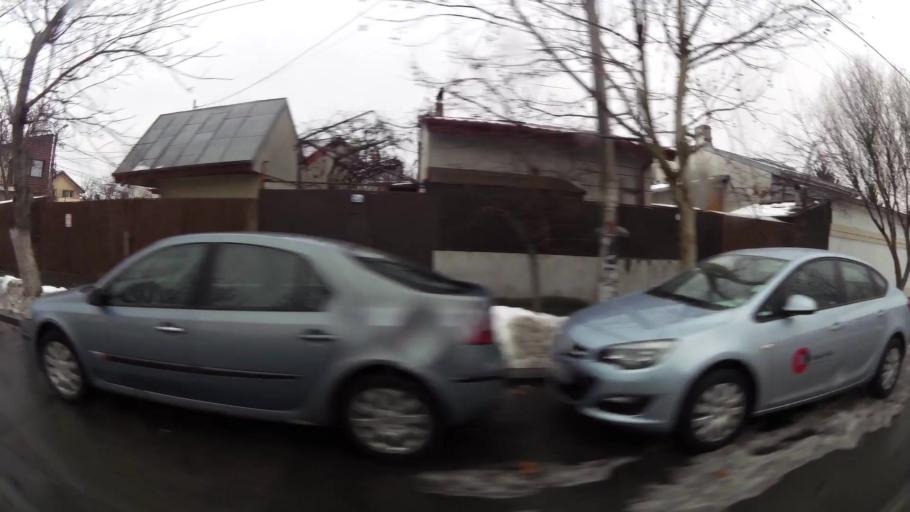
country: RO
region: Ilfov
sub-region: Comuna Chitila
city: Chitila
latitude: 44.4916
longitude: 26.0204
